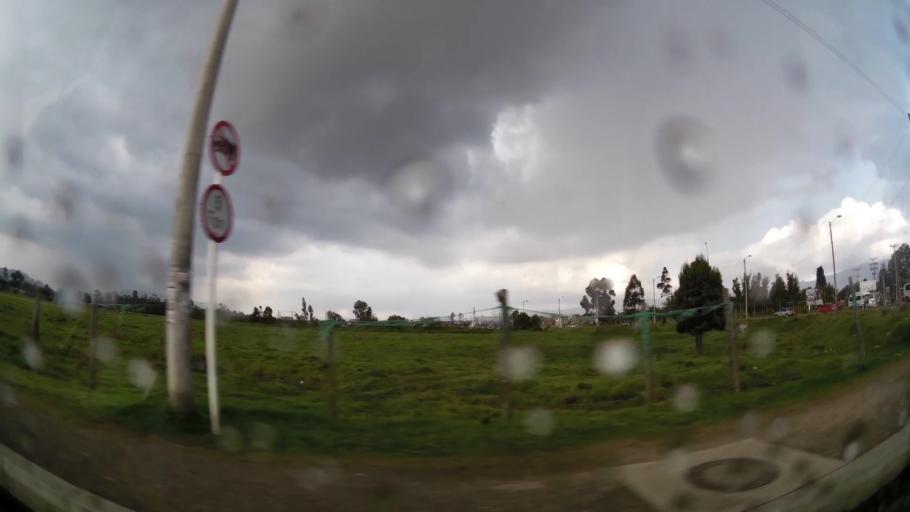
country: CO
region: Cundinamarca
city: Chia
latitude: 4.8548
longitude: -74.0683
